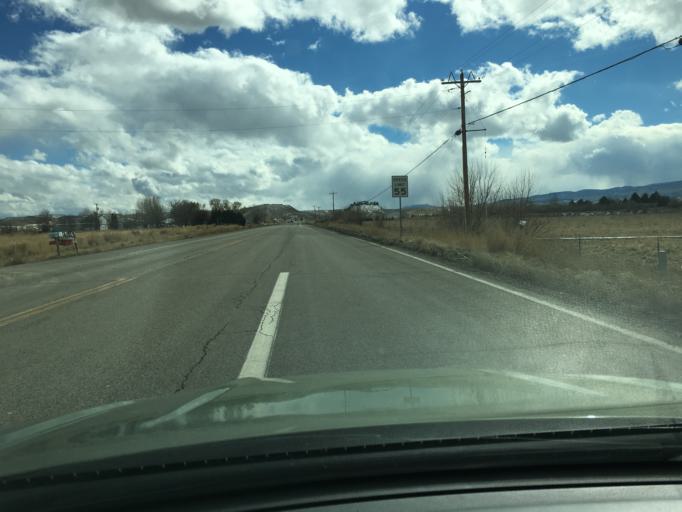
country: US
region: Colorado
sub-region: Mesa County
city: Clifton
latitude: 39.0330
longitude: -108.4596
